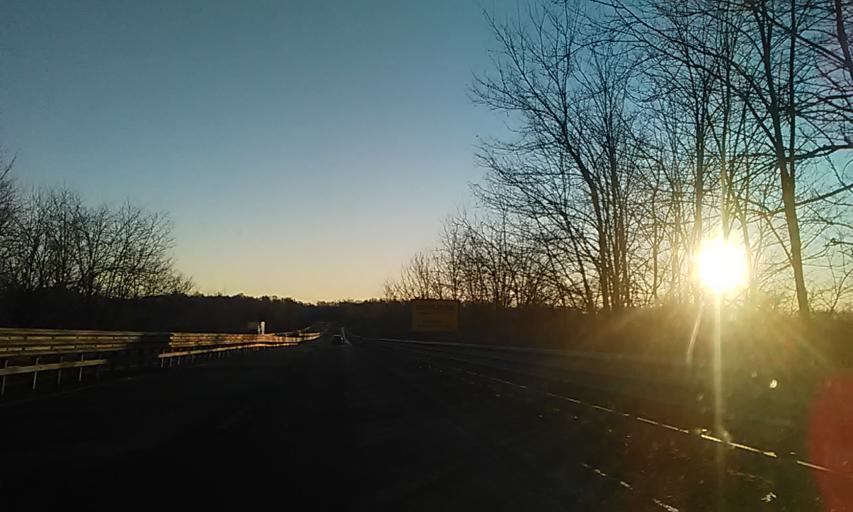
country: IT
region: Piedmont
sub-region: Provincia di Biella
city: Castelletto Cervo
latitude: 45.5519
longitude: 8.2309
